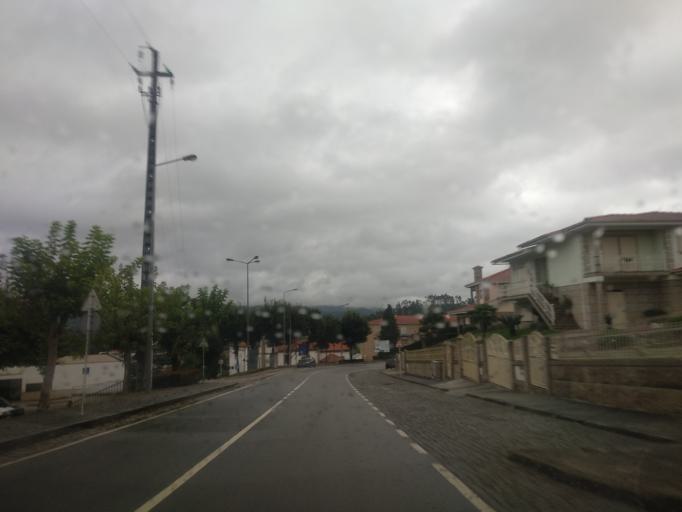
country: PT
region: Braga
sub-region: Guimaraes
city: Ponte
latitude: 41.4867
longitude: -8.3170
